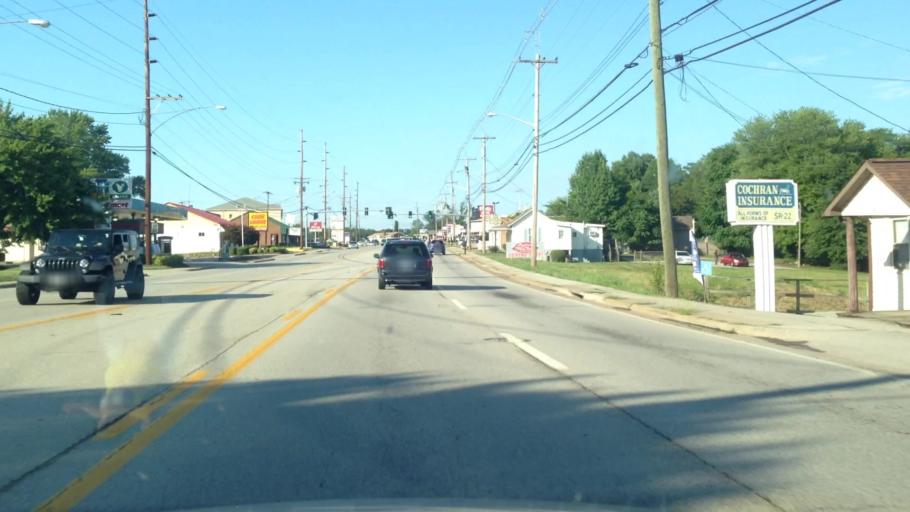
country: US
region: Virginia
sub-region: City of Danville
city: Danville
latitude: 36.6077
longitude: -79.4092
